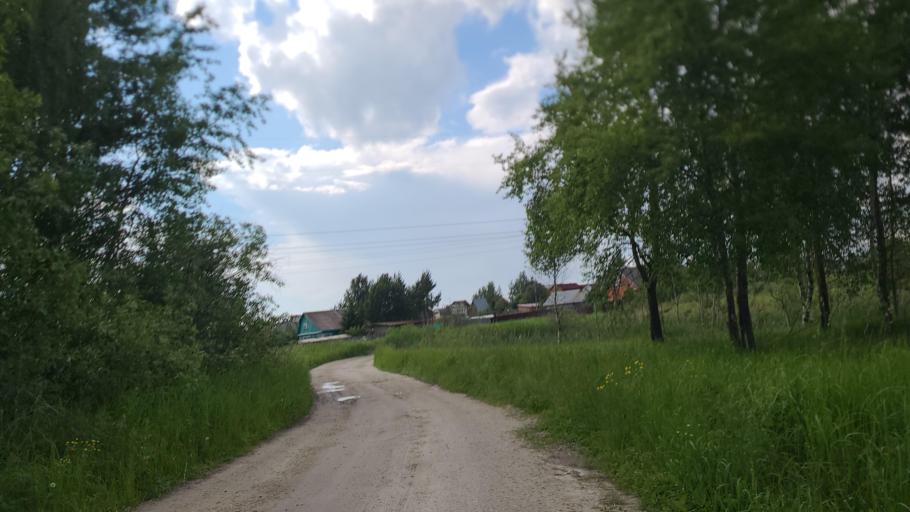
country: RU
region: Moskovskaya
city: Konobeyevo
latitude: 55.4024
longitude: 38.6747
